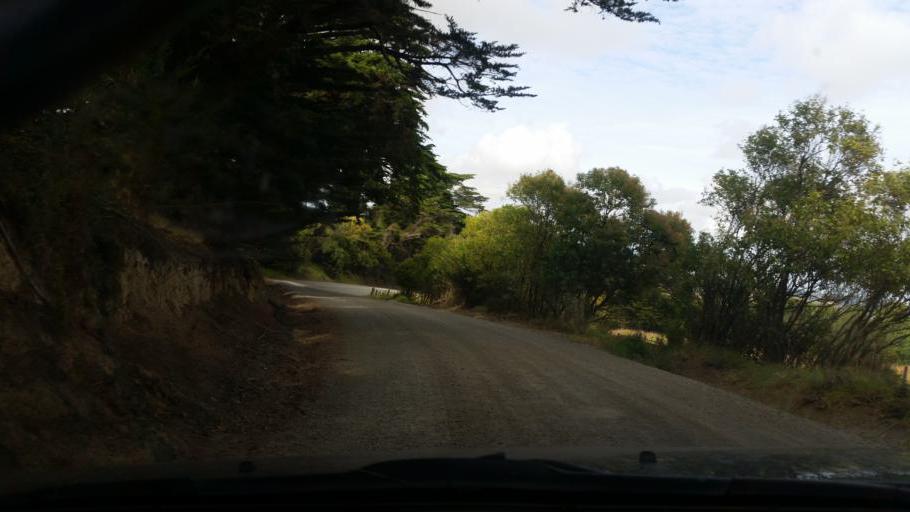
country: NZ
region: Northland
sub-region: Kaipara District
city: Dargaville
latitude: -35.9963
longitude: 173.9506
